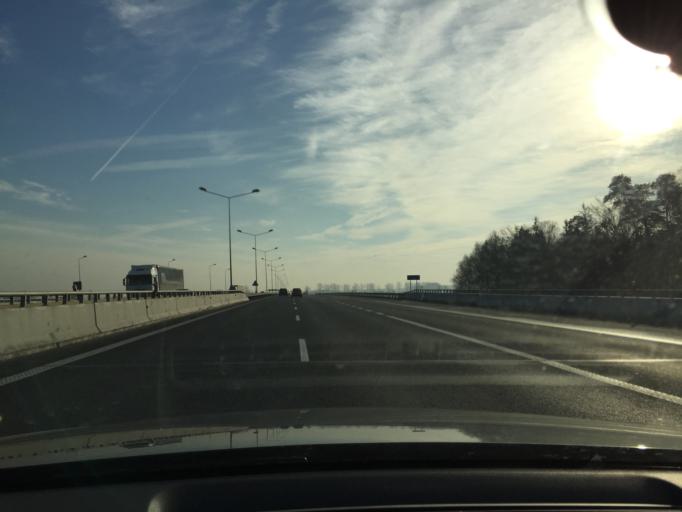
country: PL
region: Silesian Voivodeship
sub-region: Powiat gliwicki
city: Sosnicowice
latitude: 50.2807
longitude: 18.5707
